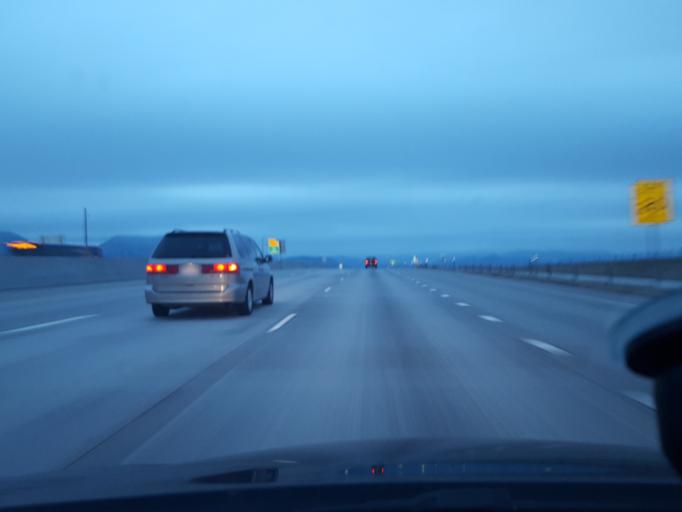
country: US
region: Colorado
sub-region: Boulder County
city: Superior
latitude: 39.9654
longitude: -105.1846
